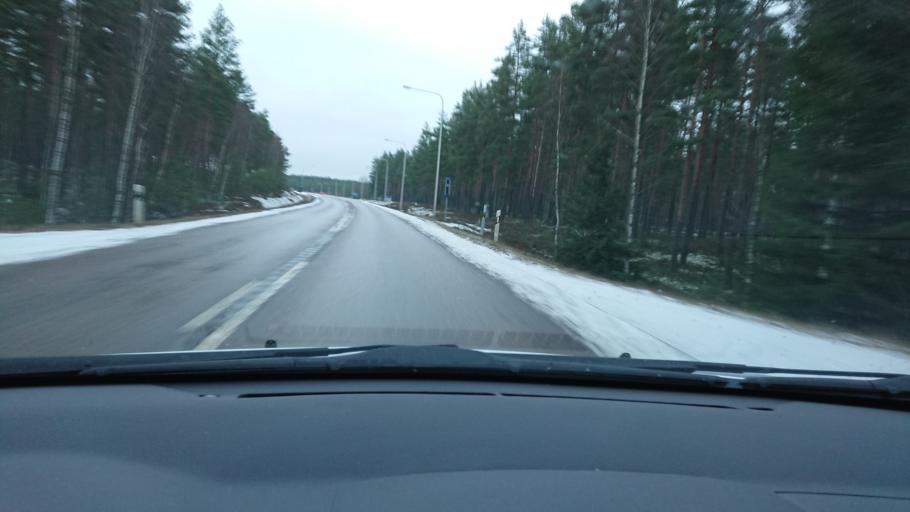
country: SE
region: Kalmar
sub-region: Hultsfreds Kommun
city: Hultsfred
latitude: 57.5154
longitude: 15.8413
